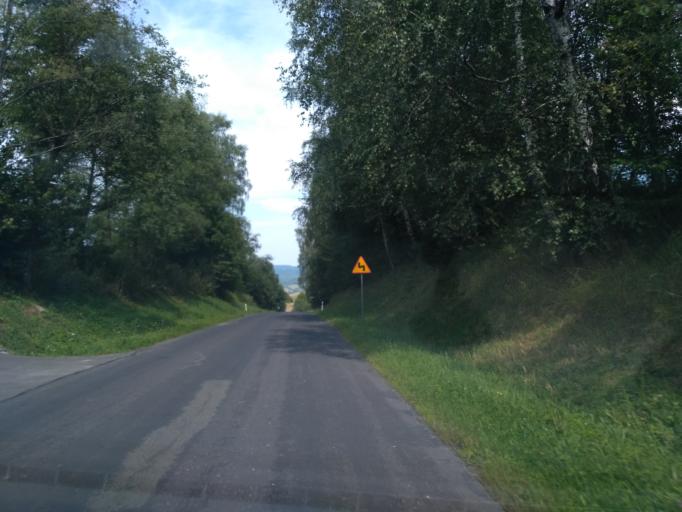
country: PL
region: Subcarpathian Voivodeship
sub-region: Powiat leski
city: Polanczyk
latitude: 49.2937
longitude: 22.5135
